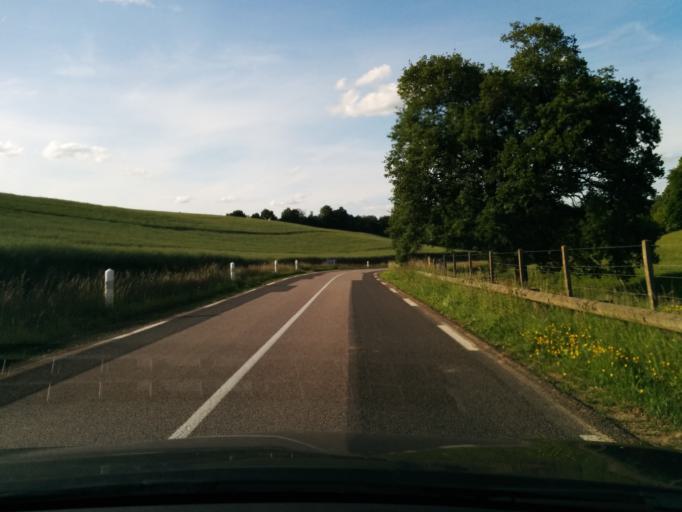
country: FR
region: Haute-Normandie
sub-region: Departement de l'Eure
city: Charleval
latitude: 49.3444
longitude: 1.4528
